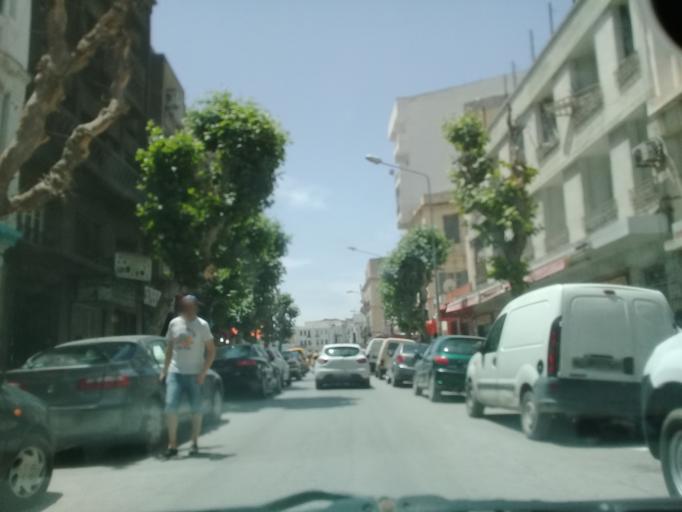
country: TN
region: Tunis
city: Tunis
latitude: 36.7936
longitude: 10.1777
